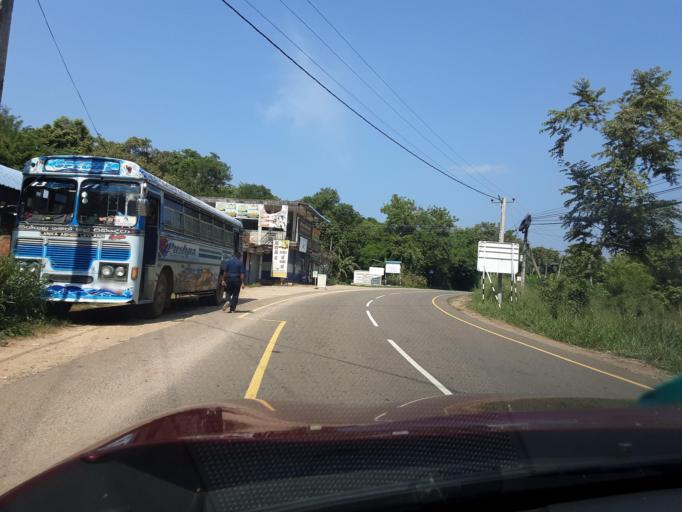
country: LK
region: Uva
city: Badulla
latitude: 7.1945
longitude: 81.0217
